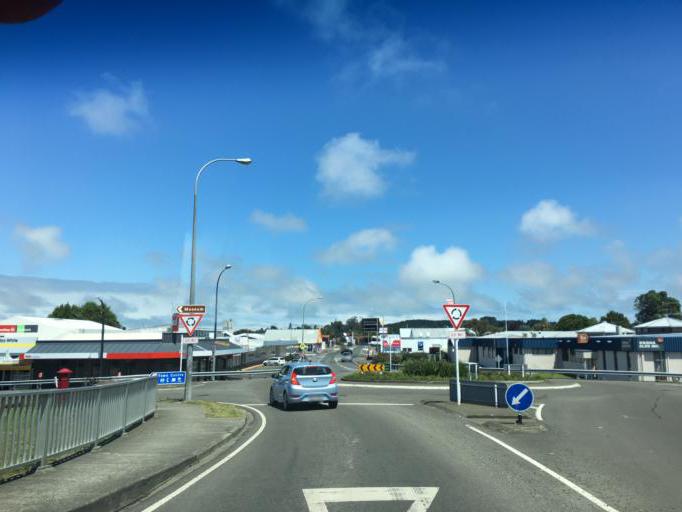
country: NZ
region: Hawke's Bay
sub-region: Wairoa District
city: Wairoa
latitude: -39.0326
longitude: 177.4185
